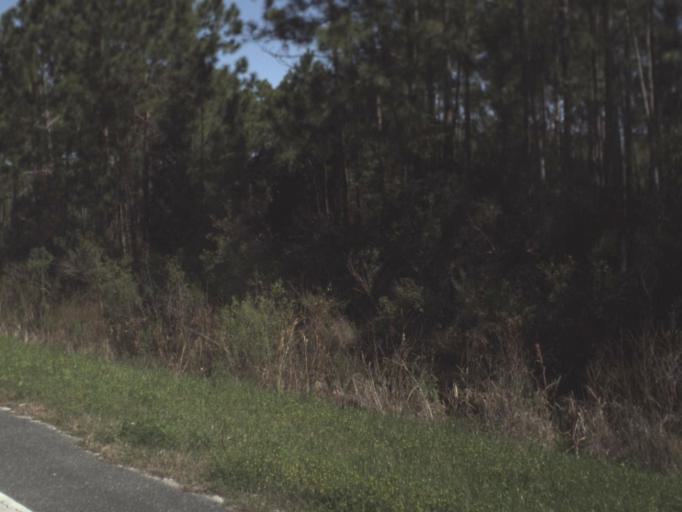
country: US
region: Florida
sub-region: Wakulla County
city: Crawfordville
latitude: 30.0419
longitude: -84.3879
